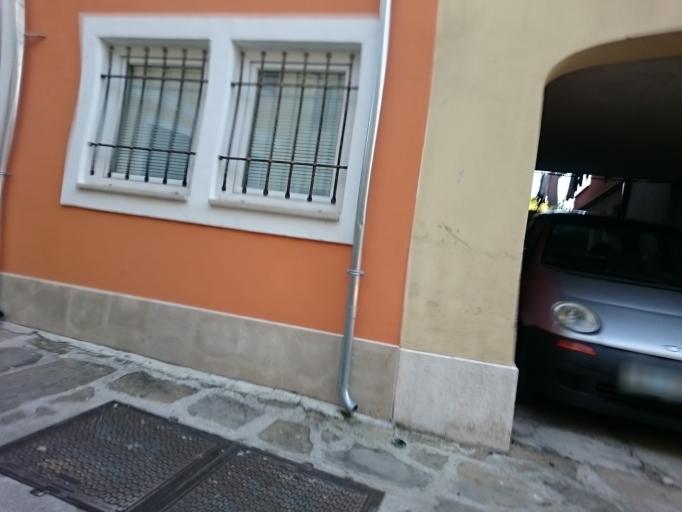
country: SI
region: Izola-Isola
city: Izola
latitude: 45.5379
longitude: 13.6602
